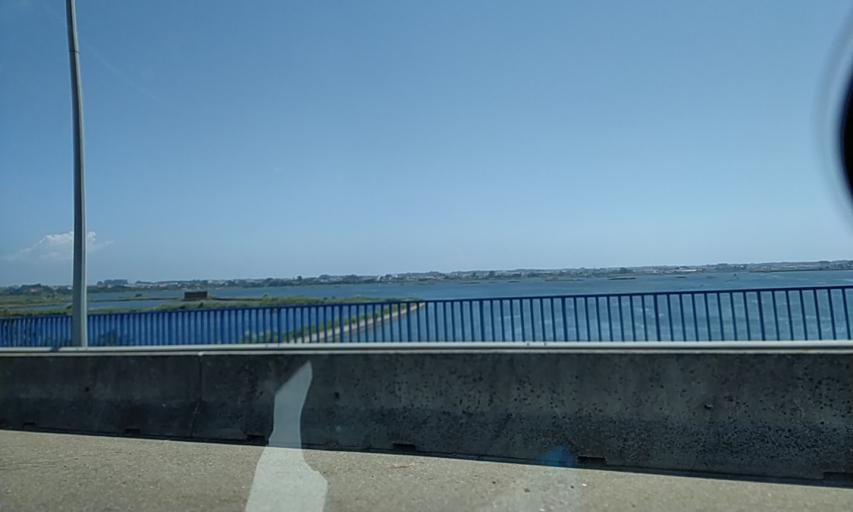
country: PT
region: Aveiro
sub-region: Ilhavo
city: Gafanha da Nazare
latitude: 40.6322
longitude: -8.6851
